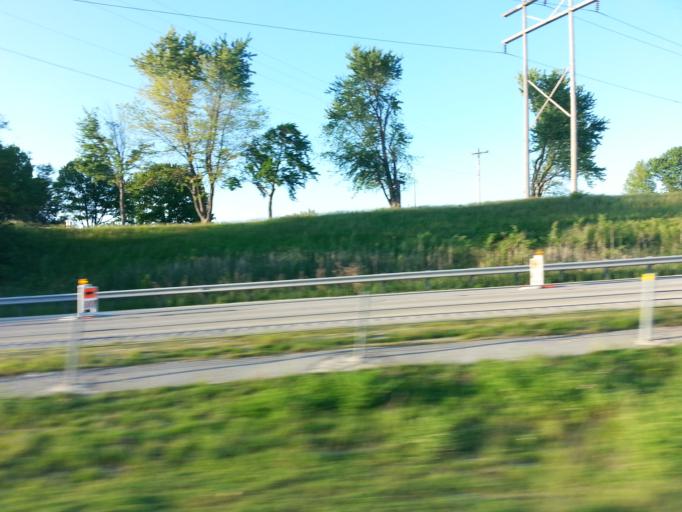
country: US
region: Illinois
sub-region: Vermilion County
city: Catlin
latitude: 40.1233
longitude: -87.7109
